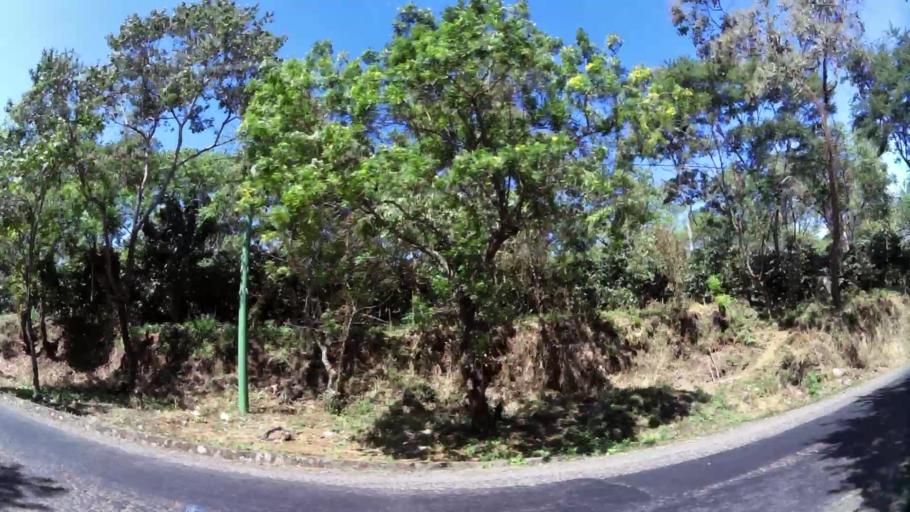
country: SV
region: Ahuachapan
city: Ahuachapan
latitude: 13.9416
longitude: -89.8266
